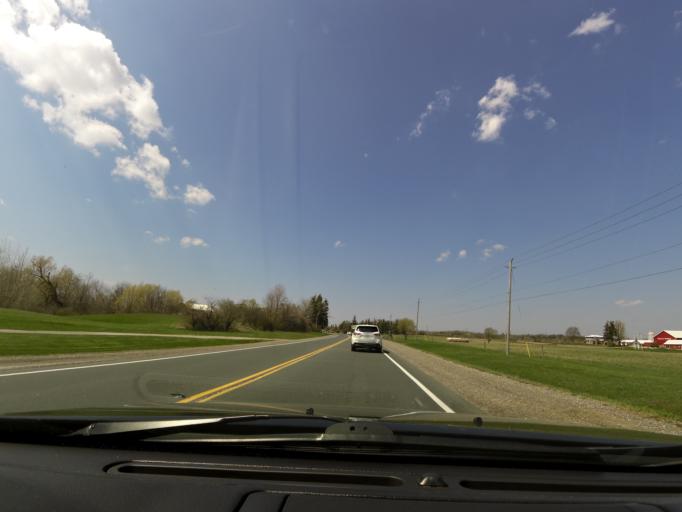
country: CA
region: Ontario
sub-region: Wellington County
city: Guelph
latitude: 43.4402
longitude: -80.1065
